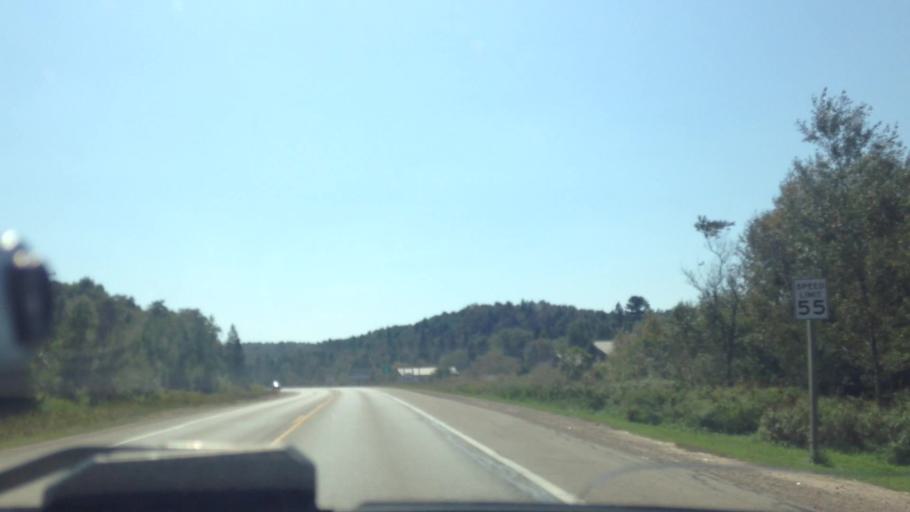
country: US
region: Michigan
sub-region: Alger County
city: Munising
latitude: 46.3977
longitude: -86.6485
